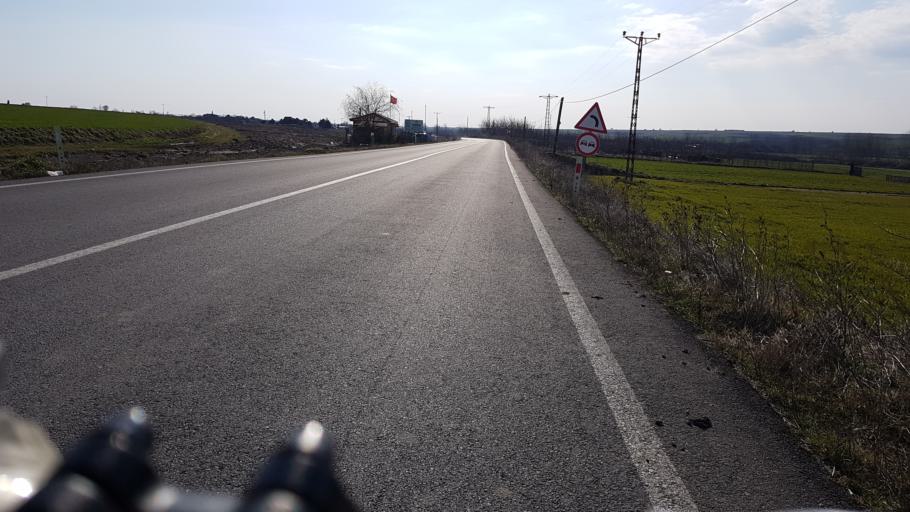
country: TR
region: Tekirdag
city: Velimese
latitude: 41.3520
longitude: 27.8421
